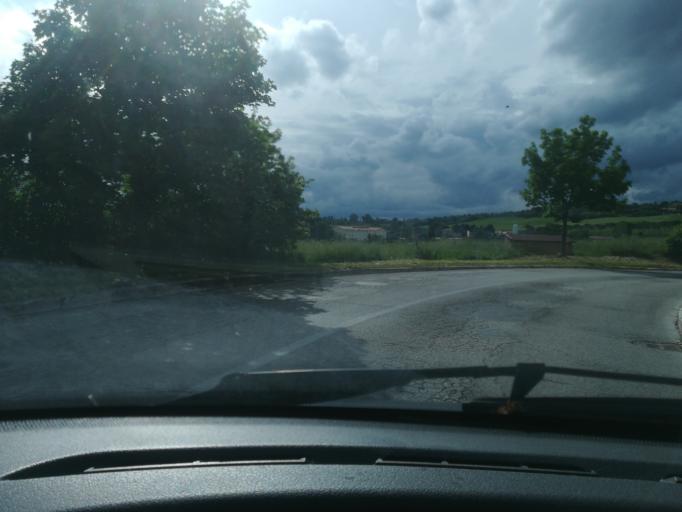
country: IT
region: The Marches
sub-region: Provincia di Macerata
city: Macerata
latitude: 43.2861
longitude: 13.4283
